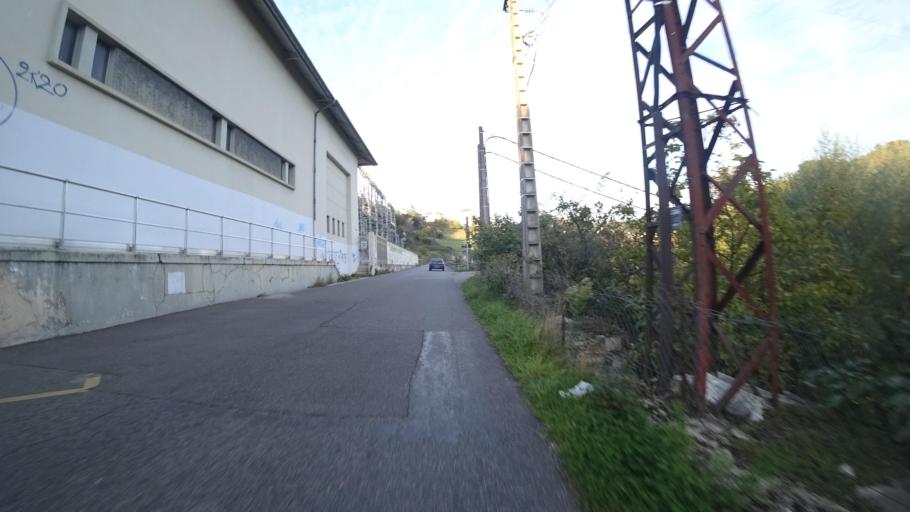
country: FR
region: Midi-Pyrenees
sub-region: Departement de l'Aveyron
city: Le Monastere
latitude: 44.3427
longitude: 2.5736
